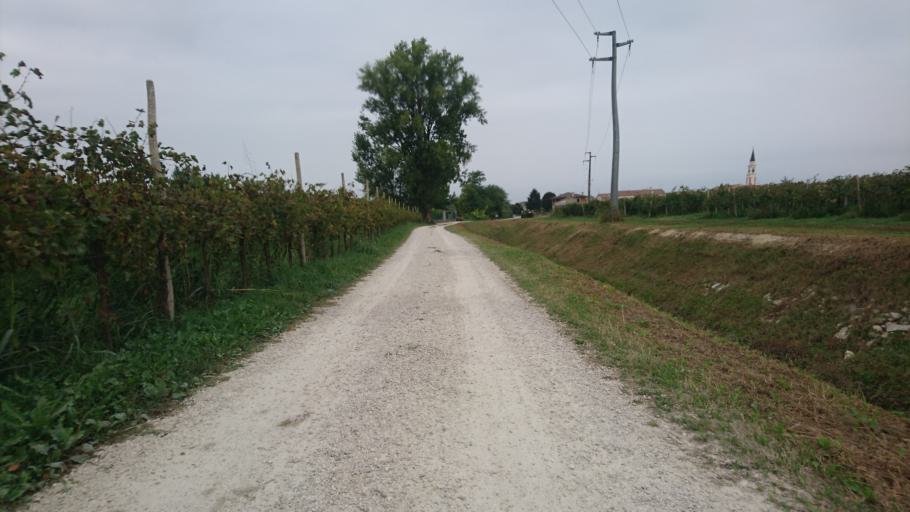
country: IT
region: Veneto
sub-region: Provincia di Padova
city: Tavo
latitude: 45.4938
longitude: 11.8568
